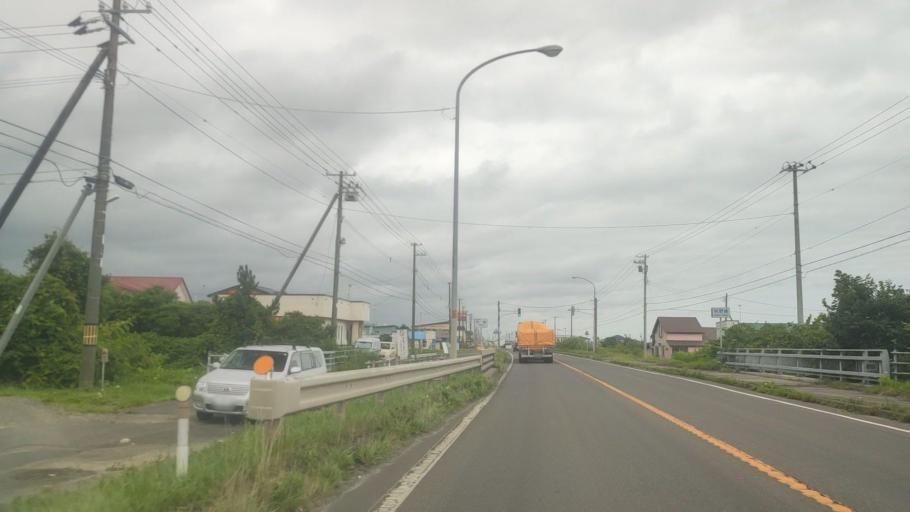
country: JP
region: Hokkaido
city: Shiraoi
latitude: 42.5116
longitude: 141.2929
